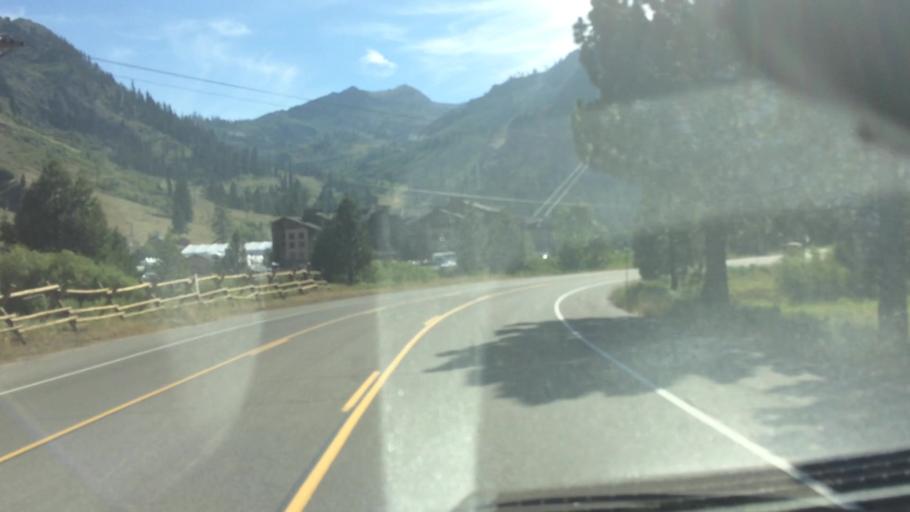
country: US
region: California
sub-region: Placer County
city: Sunnyside-Tahoe City
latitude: 39.1988
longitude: -120.2301
